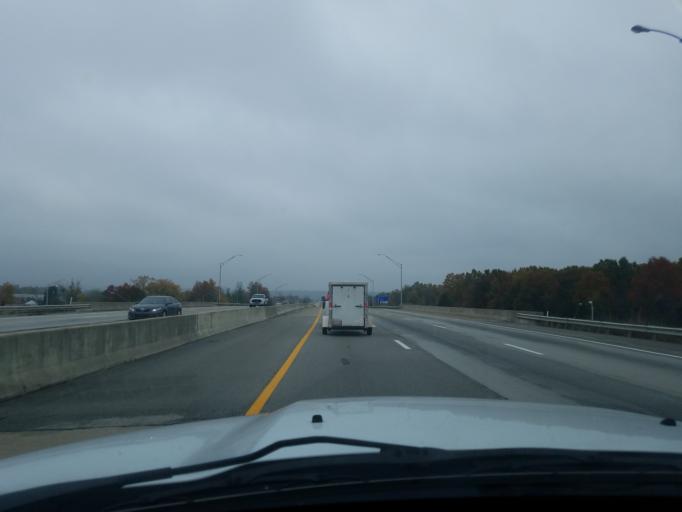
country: US
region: Kentucky
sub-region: Bullitt County
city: Shepherdsville
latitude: 37.9780
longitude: -85.6974
